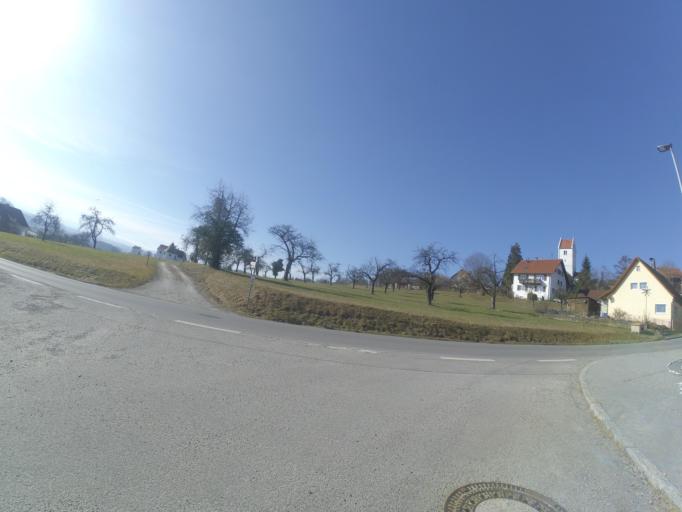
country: DE
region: Baden-Wuerttemberg
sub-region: Tuebingen Region
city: Wolpertswende
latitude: 47.8941
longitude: 9.6151
